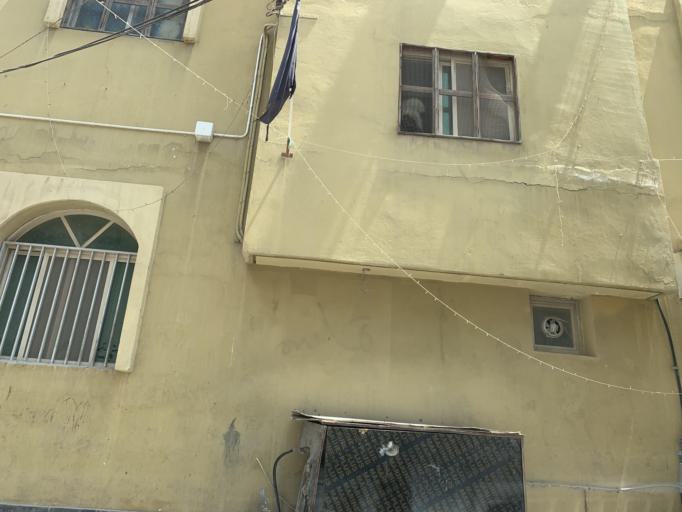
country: BH
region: Manama
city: Jidd Hafs
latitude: 26.2053
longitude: 50.5526
